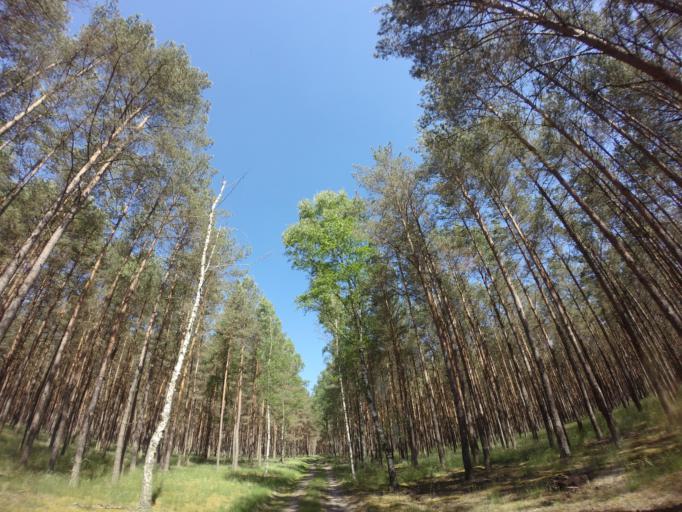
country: PL
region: West Pomeranian Voivodeship
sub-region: Powiat drawski
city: Kalisz Pomorski
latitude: 53.1840
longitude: 15.9820
